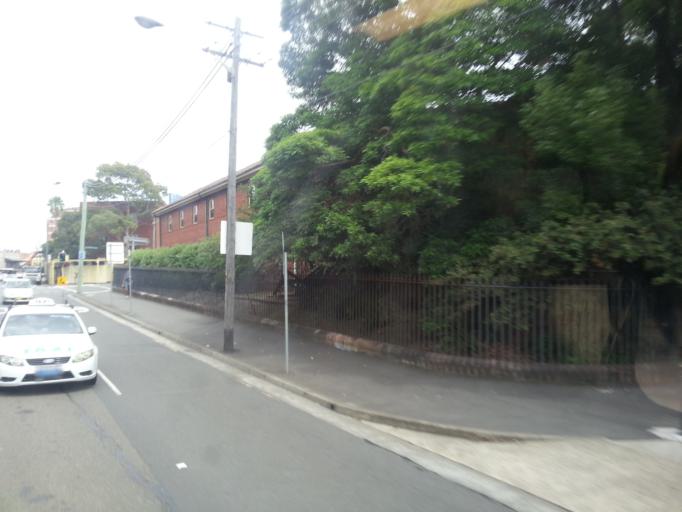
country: AU
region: New South Wales
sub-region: City of Sydney
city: Darlington
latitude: -33.8910
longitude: 151.1886
